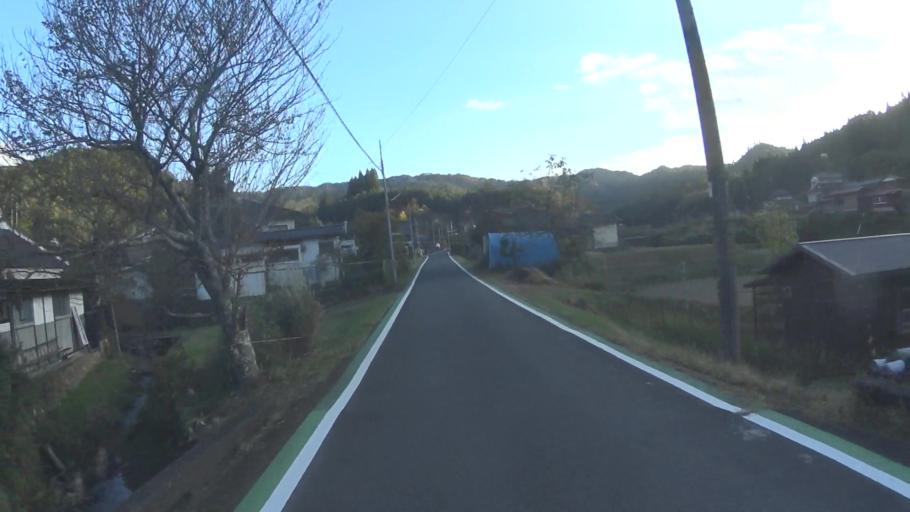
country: JP
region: Kyoto
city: Ayabe
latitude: 35.2817
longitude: 135.2504
